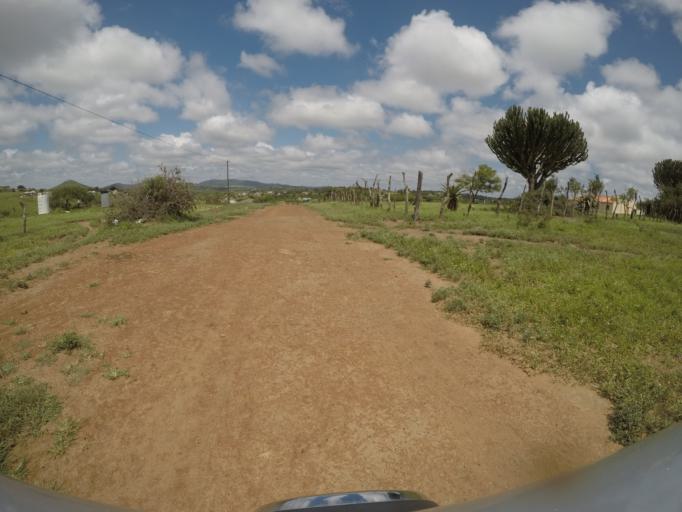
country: ZA
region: KwaZulu-Natal
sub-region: uThungulu District Municipality
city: Empangeni
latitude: -28.5769
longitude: 31.8385
